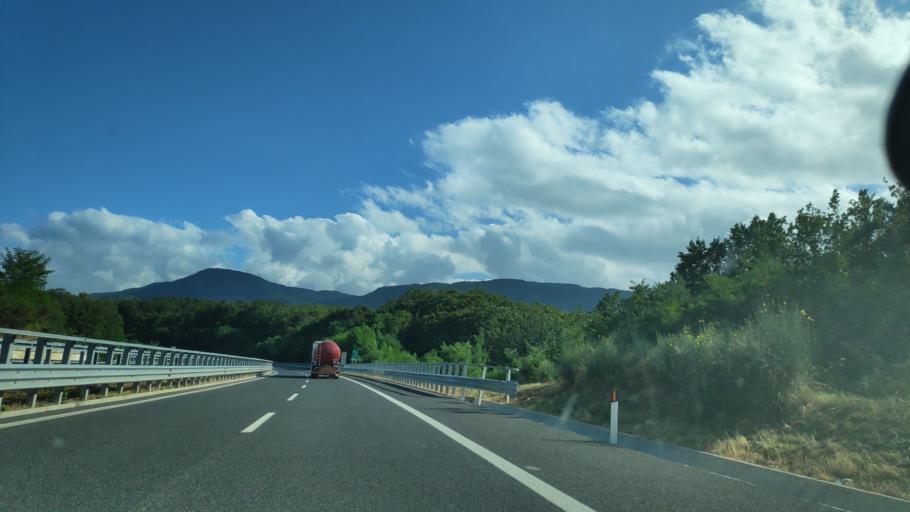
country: IT
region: Campania
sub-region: Provincia di Salerno
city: Casalbuono
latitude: 40.2412
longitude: 15.6596
